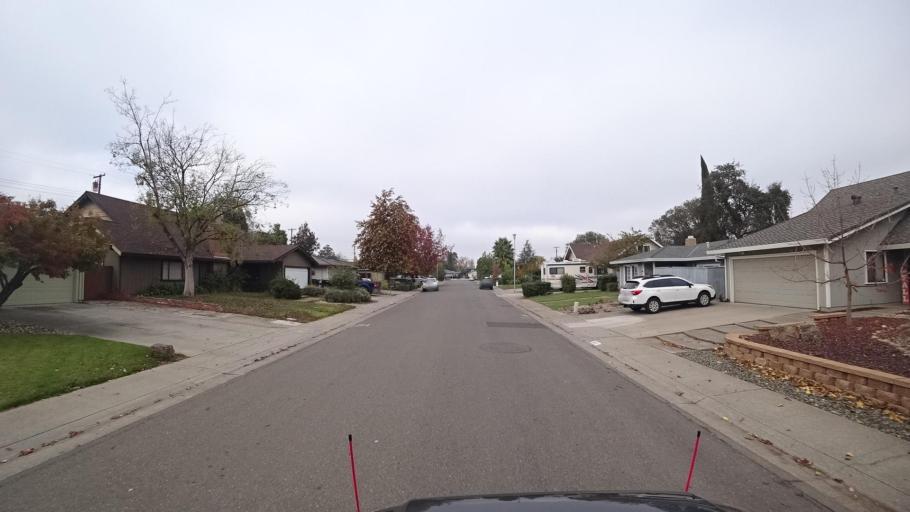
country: US
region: California
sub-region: Sacramento County
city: Elk Grove
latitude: 38.4114
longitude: -121.3697
